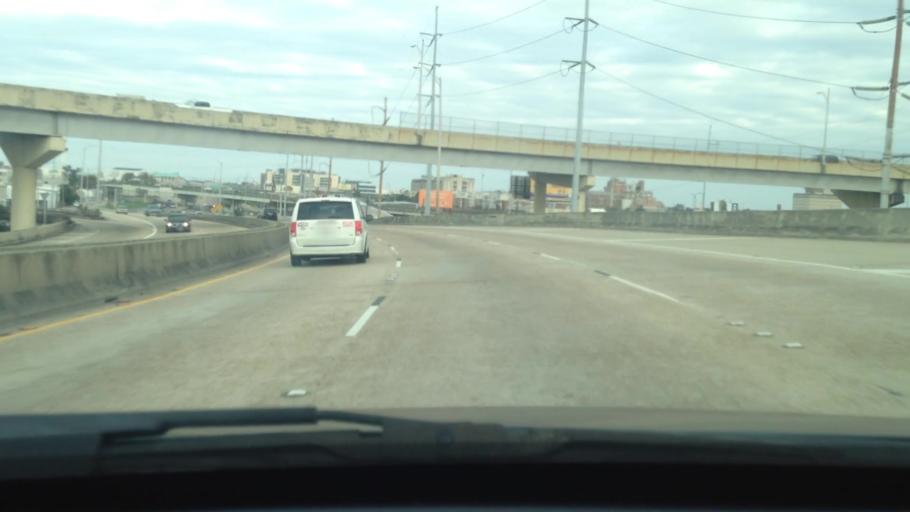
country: US
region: Louisiana
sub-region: Orleans Parish
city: New Orleans
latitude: 29.9522
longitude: -90.0860
